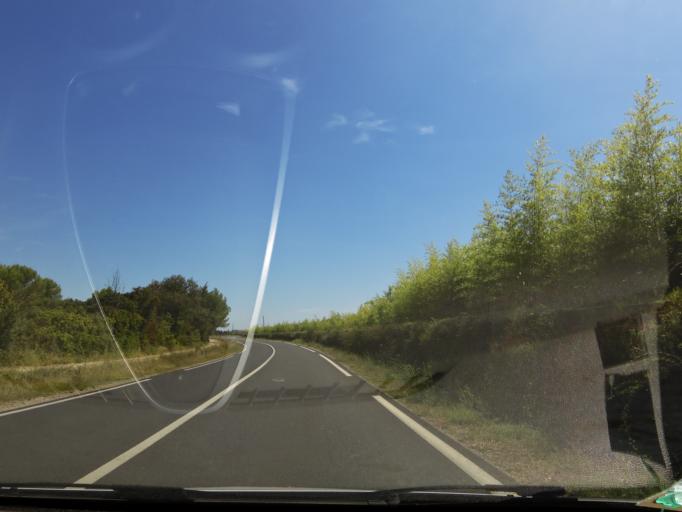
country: FR
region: Languedoc-Roussillon
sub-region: Departement de l'Herault
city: Vendargues
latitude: 43.6652
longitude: 3.9778
